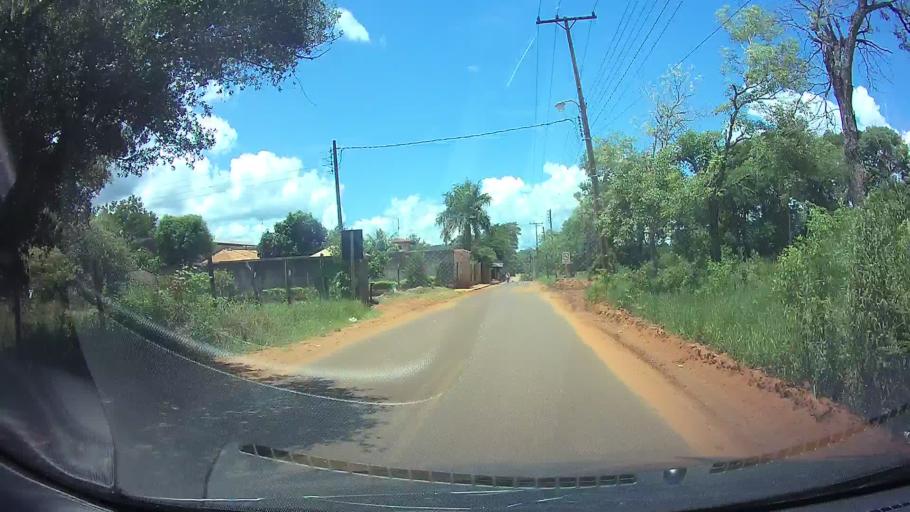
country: PY
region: Central
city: Itaugua
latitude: -25.3739
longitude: -57.3657
